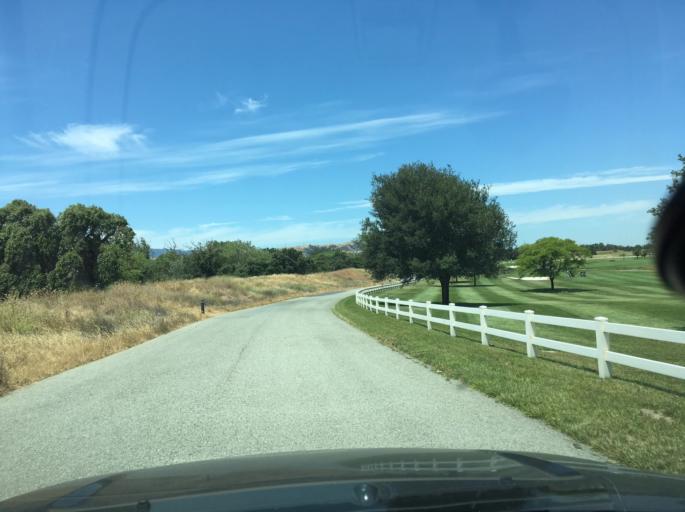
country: US
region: California
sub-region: Santa Clara County
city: Morgan Hill
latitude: 37.1895
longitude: -121.7010
